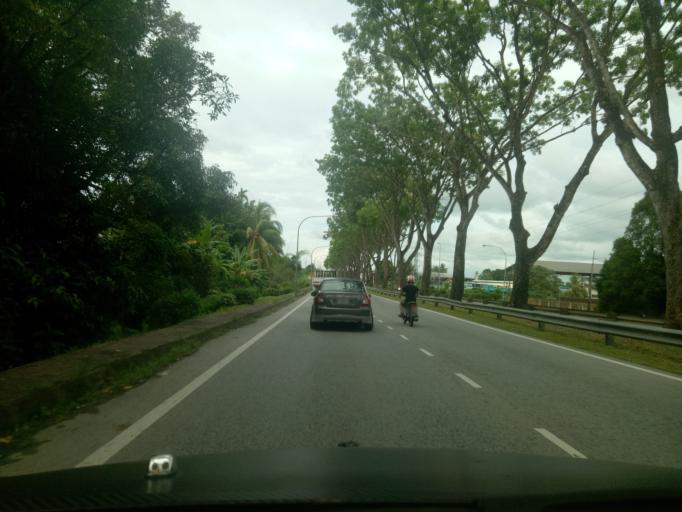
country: MY
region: Sarawak
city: Kuching
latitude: 1.5453
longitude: 110.3766
